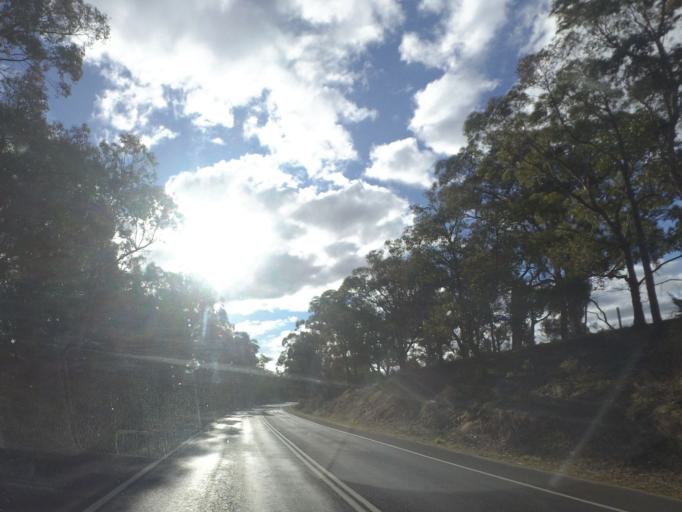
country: AU
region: Victoria
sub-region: Mount Alexander
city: Castlemaine
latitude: -37.1219
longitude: 144.3417
